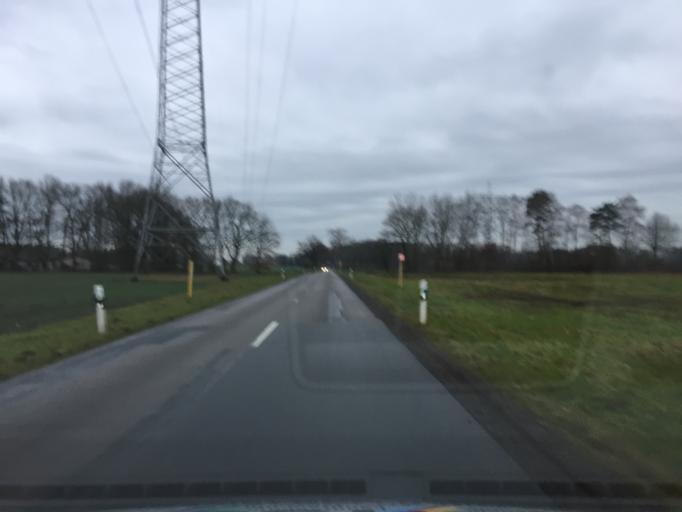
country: DE
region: Lower Saxony
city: Pennigsehl
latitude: 52.6203
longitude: 8.9959
